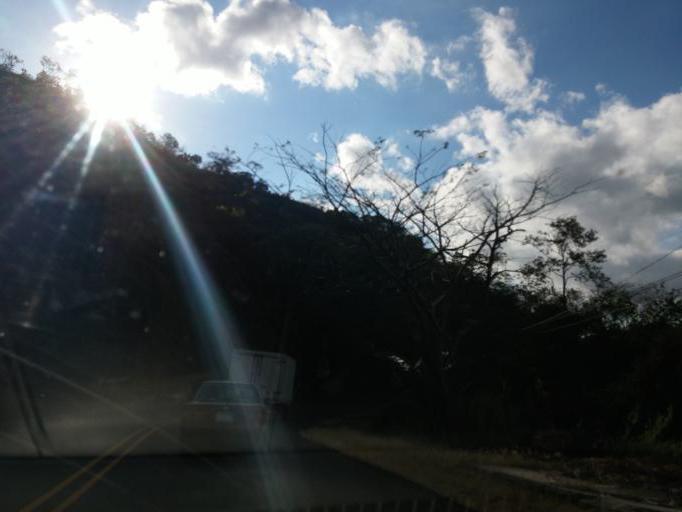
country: CR
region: San Jose
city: San Ignacio
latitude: 9.7982
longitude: -84.1581
